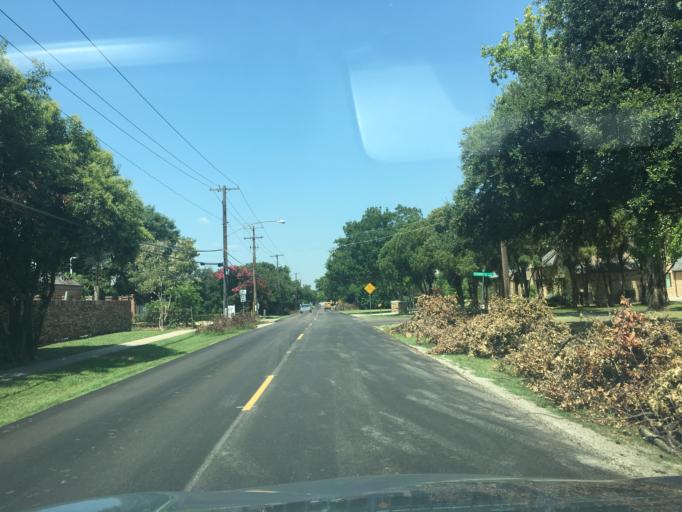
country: US
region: Texas
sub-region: Dallas County
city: Addison
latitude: 32.9170
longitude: -96.7942
